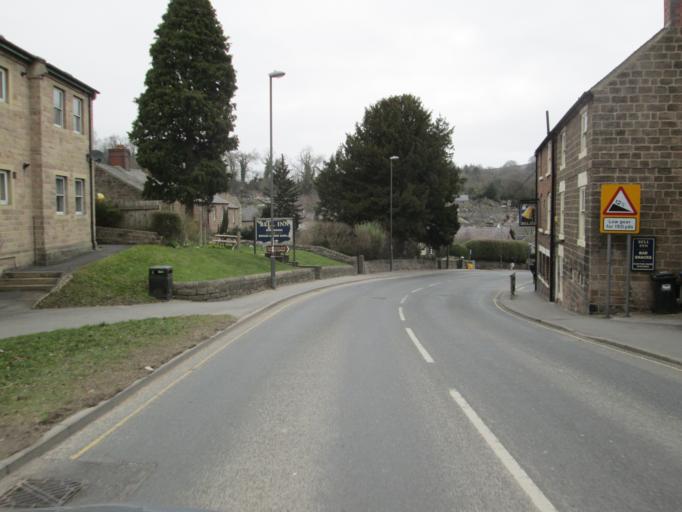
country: GB
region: England
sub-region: Derbyshire
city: Cromford
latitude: 53.1071
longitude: -1.5625
